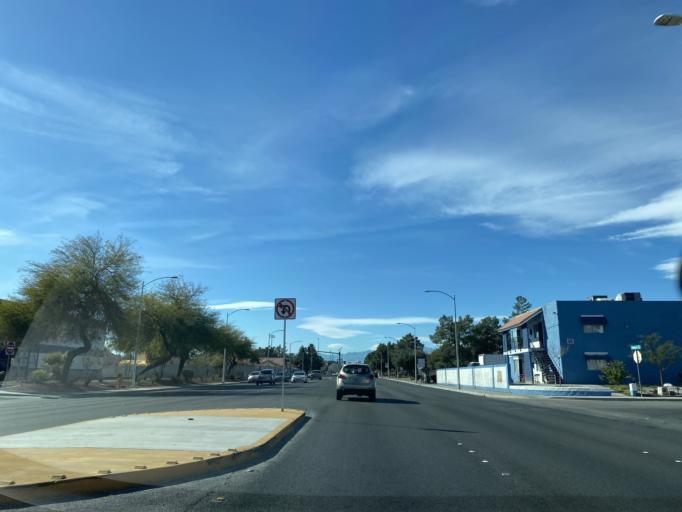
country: US
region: Nevada
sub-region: Clark County
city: Sunrise Manor
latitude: 36.1735
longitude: -115.0863
